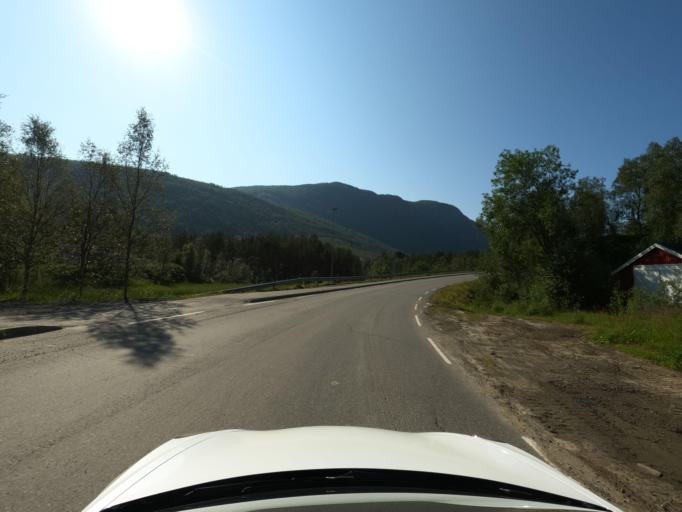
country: NO
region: Nordland
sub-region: Narvik
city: Bjerkvik
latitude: 68.3715
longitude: 17.6017
